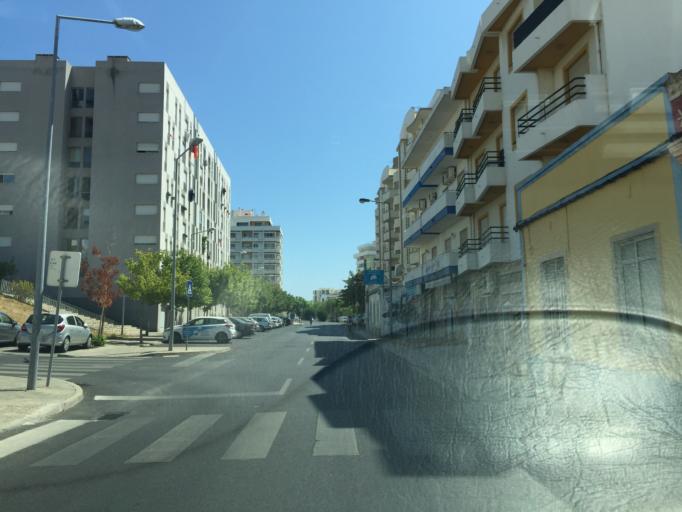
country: PT
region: Faro
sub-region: Faro
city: Faro
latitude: 37.0268
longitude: -7.9399
